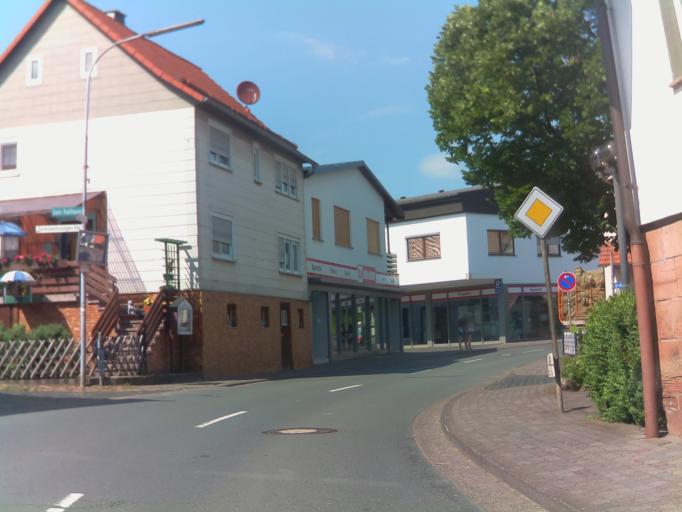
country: DE
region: Hesse
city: Rosenthal
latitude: 50.9745
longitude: 8.8686
